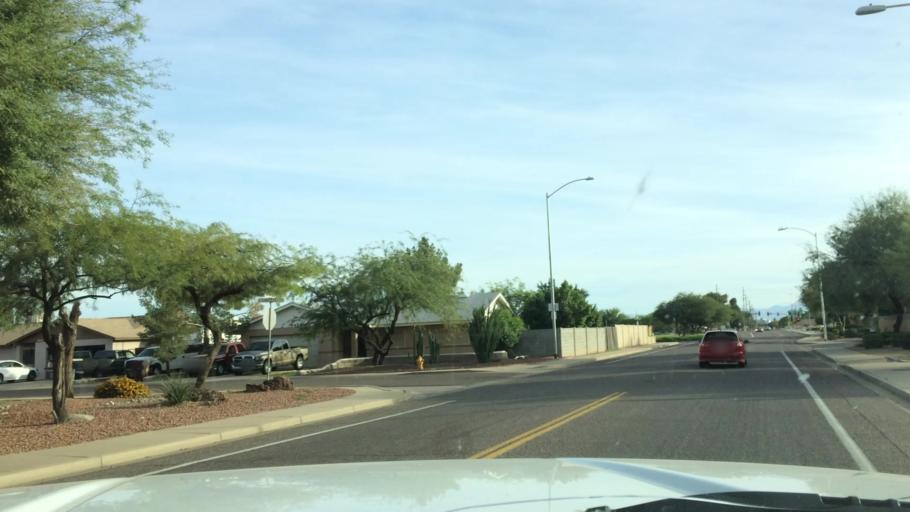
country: US
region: Arizona
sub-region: Maricopa County
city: Peoria
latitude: 33.5692
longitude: -112.2638
